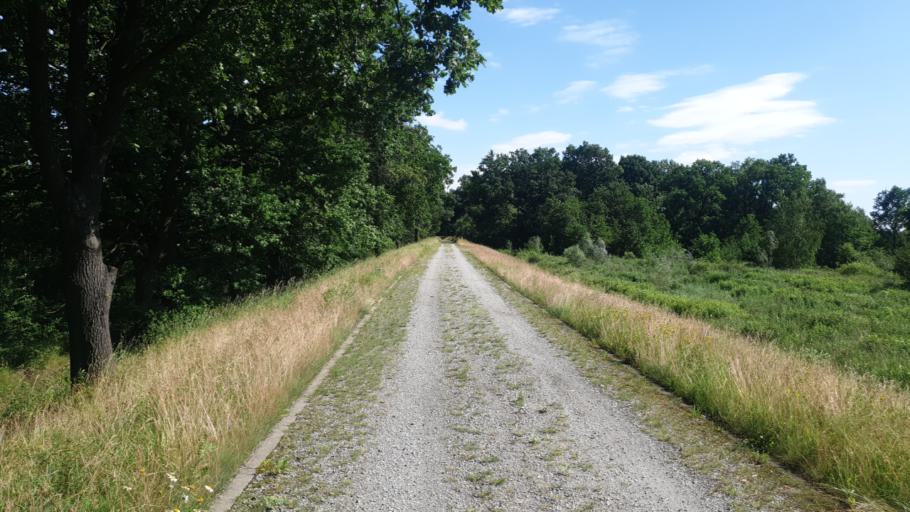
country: PL
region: Lower Silesian Voivodeship
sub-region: Powiat wroclawski
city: Radwanice
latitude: 51.0875
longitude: 17.1166
